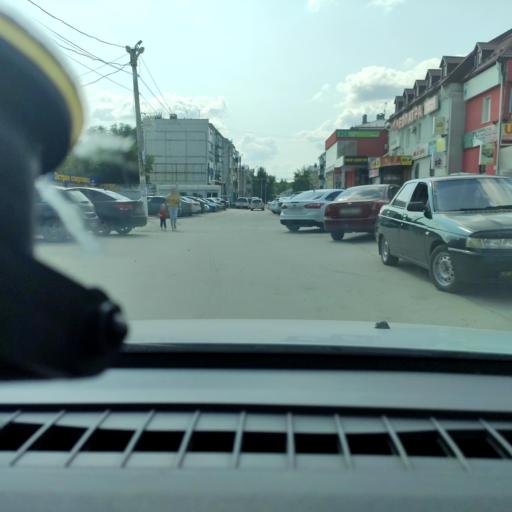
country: RU
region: Samara
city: Chapayevsk
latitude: 52.9543
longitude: 49.6902
